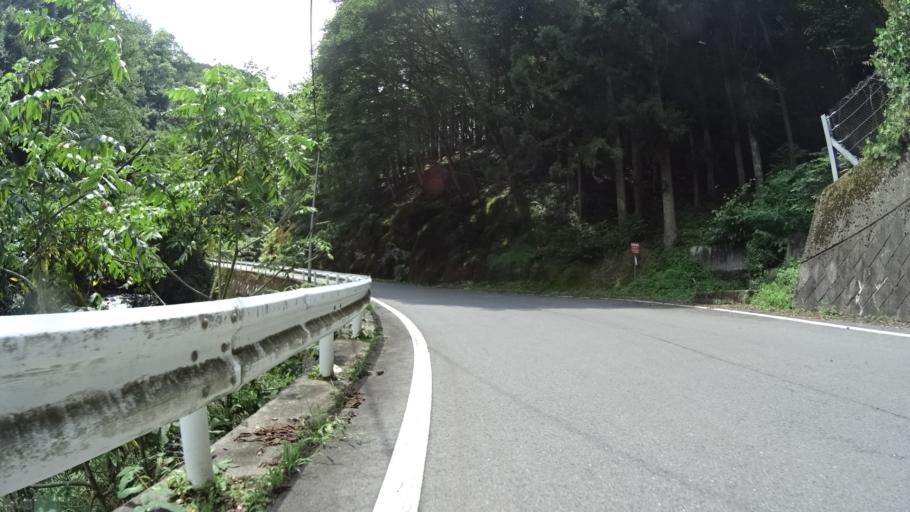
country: JP
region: Nagano
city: Saku
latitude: 36.0679
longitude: 138.6991
